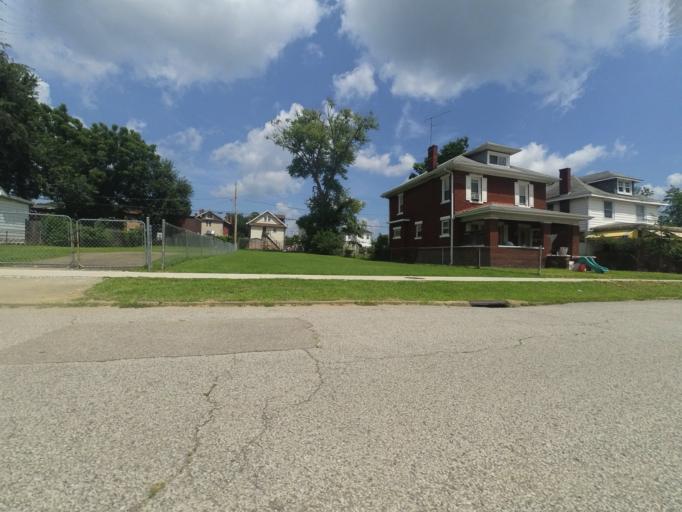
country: US
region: West Virginia
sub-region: Cabell County
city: Huntington
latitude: 38.4158
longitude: -82.4244
